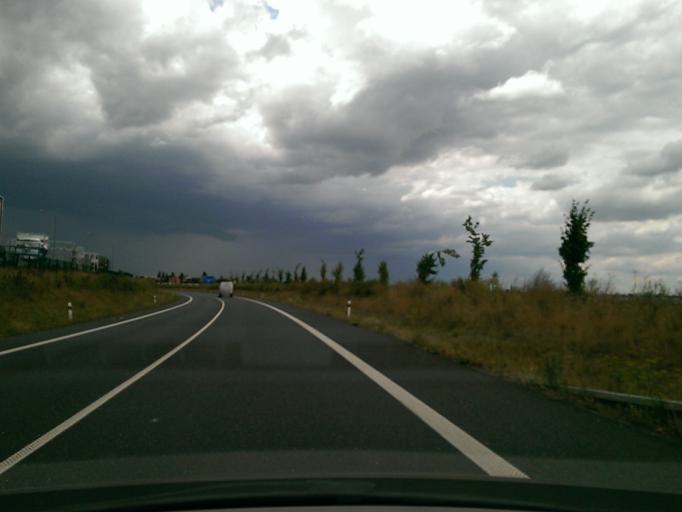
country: CZ
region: Central Bohemia
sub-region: Okres Nymburk
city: Nymburk
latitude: 50.2039
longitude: 15.0448
